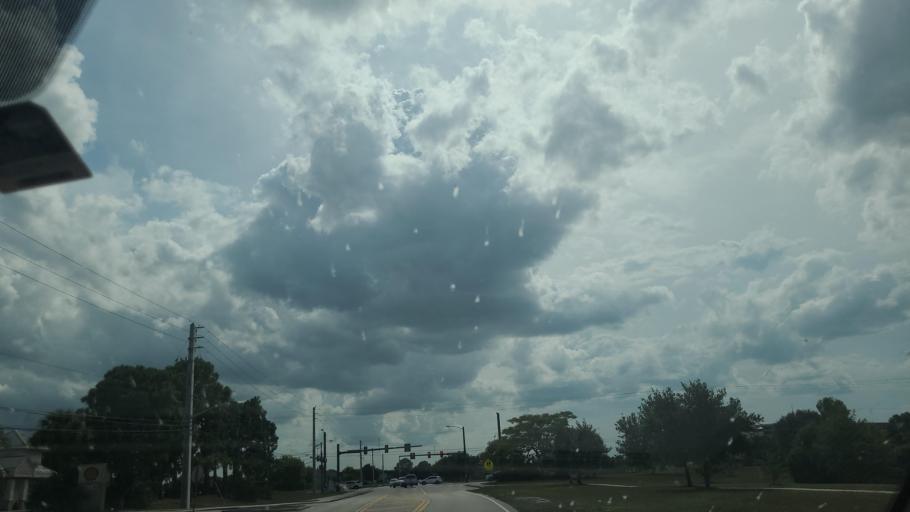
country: US
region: Florida
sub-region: Saint Lucie County
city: Port Saint Lucie
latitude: 27.2439
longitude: -80.3612
